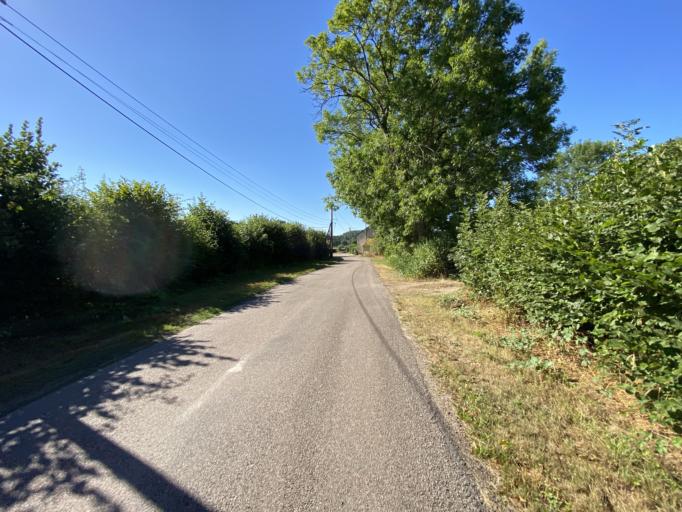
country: FR
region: Bourgogne
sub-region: Departement de la Cote-d'Or
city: Saulieu
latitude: 47.2625
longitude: 4.1769
